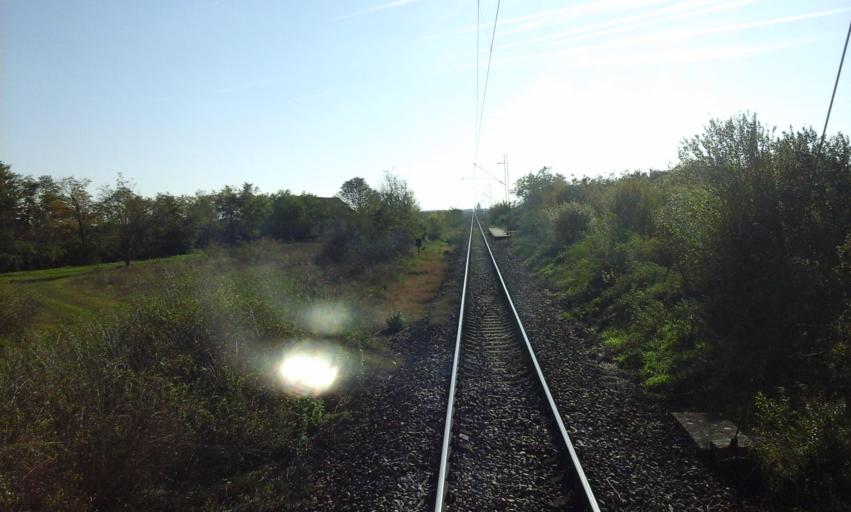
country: RS
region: Autonomna Pokrajina Vojvodina
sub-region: Severnobacki Okrug
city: Subotica
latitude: 45.9869
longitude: 19.6755
